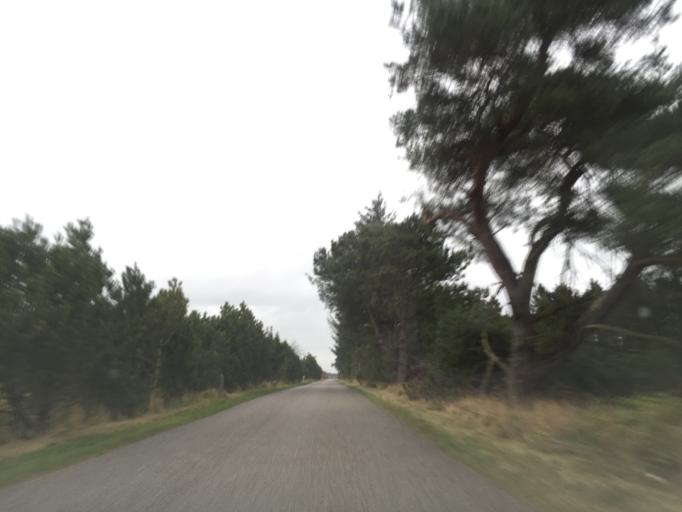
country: DK
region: Central Jutland
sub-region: Silkeborg Kommune
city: Svejbaek
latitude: 56.1896
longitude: 9.6436
